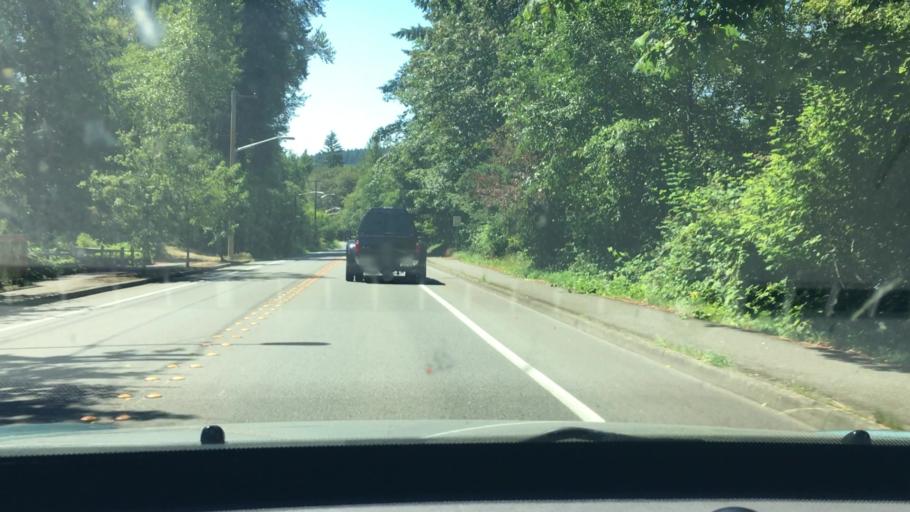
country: US
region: Washington
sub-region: King County
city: Newcastle
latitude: 47.5457
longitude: -122.1296
